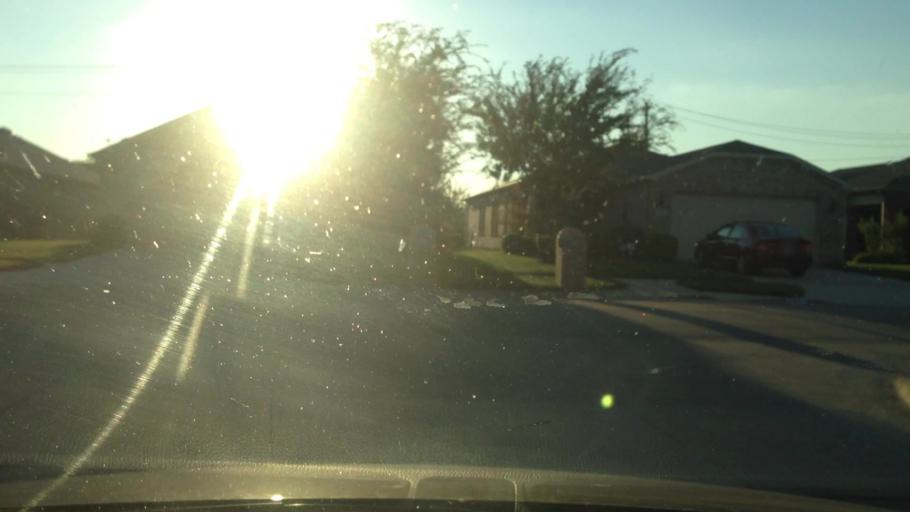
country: US
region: Texas
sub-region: Denton County
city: Little Elm
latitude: 33.1398
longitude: -96.9217
